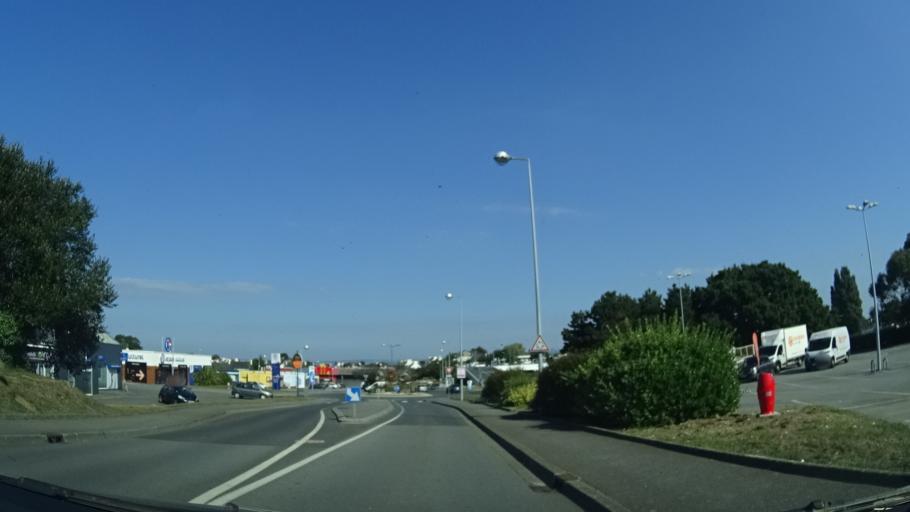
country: FR
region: Brittany
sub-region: Departement du Finistere
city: Douarnenez
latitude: 48.0902
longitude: -4.3467
